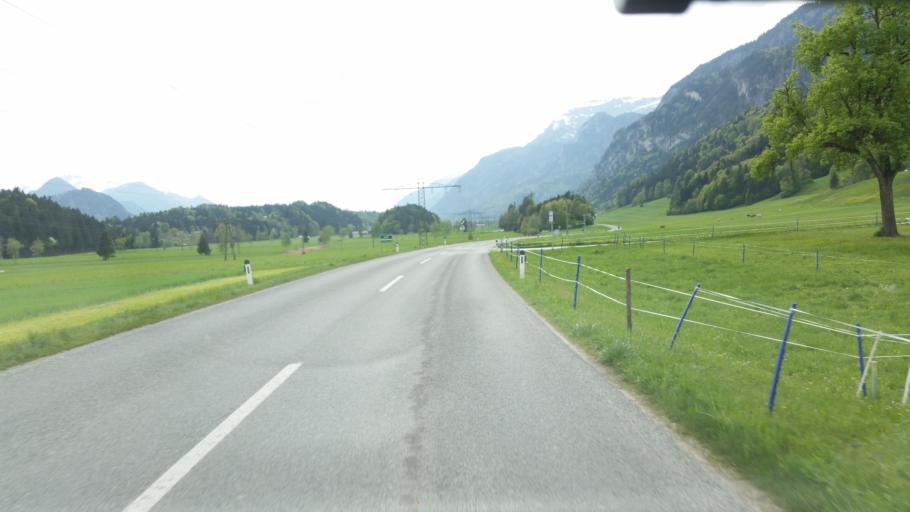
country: AT
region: Tyrol
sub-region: Politischer Bezirk Kufstein
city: Radfeld
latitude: 47.4725
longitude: 11.9324
